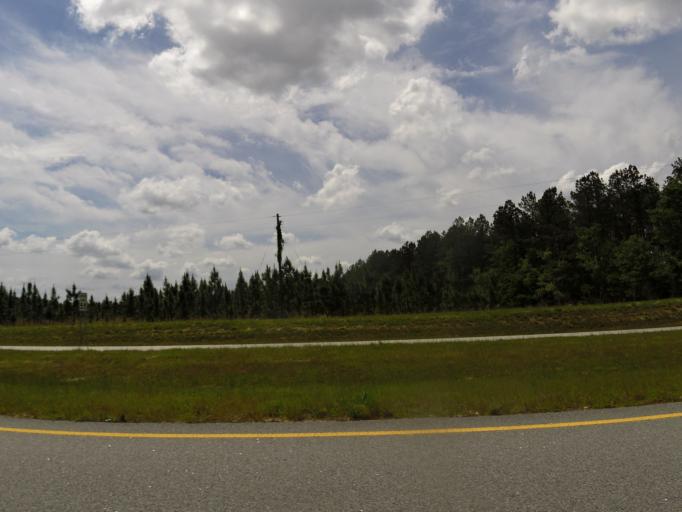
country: US
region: Georgia
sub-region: Emanuel County
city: Swainsboro
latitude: 32.7010
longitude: -82.3908
